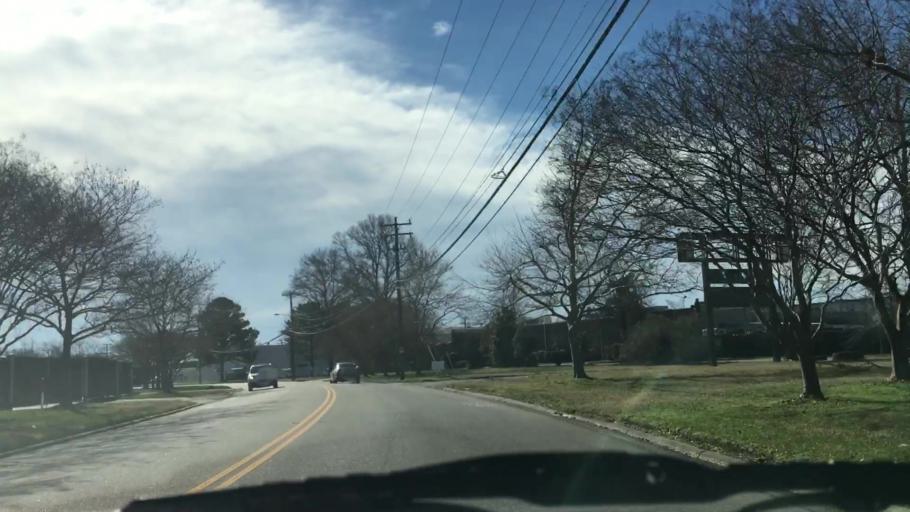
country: US
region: Virginia
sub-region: City of Norfolk
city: Norfolk
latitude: 36.8654
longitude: -76.2355
